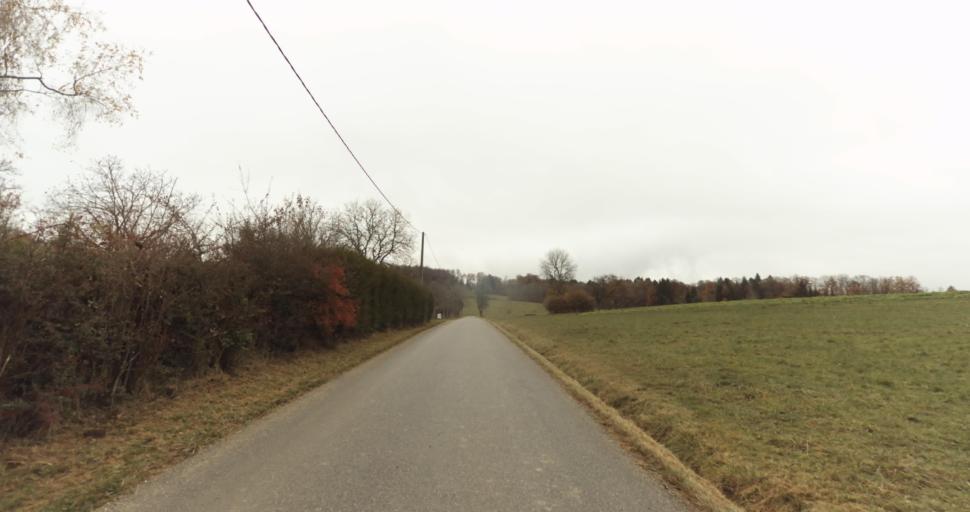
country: FR
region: Rhone-Alpes
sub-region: Departement de la Haute-Savoie
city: Groisy
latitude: 46.0263
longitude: 6.1980
